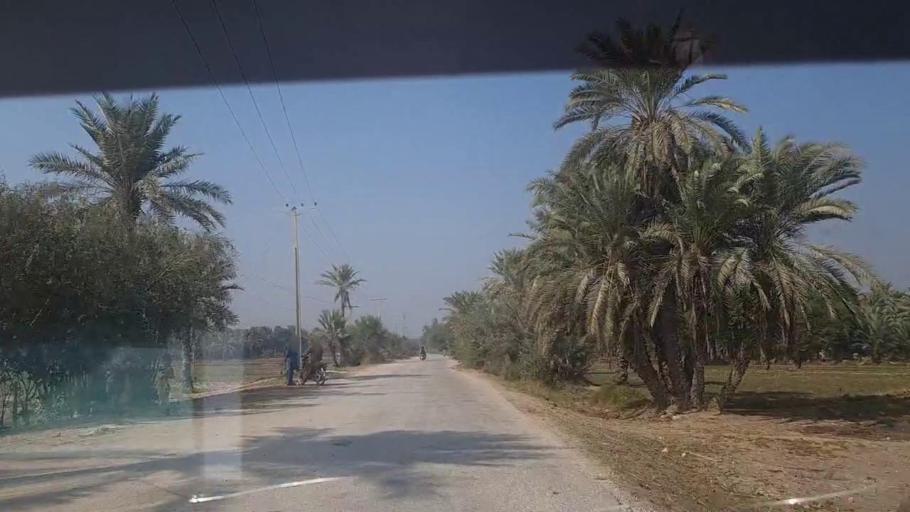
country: PK
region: Sindh
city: Kot Diji
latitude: 27.3625
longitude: 68.7064
